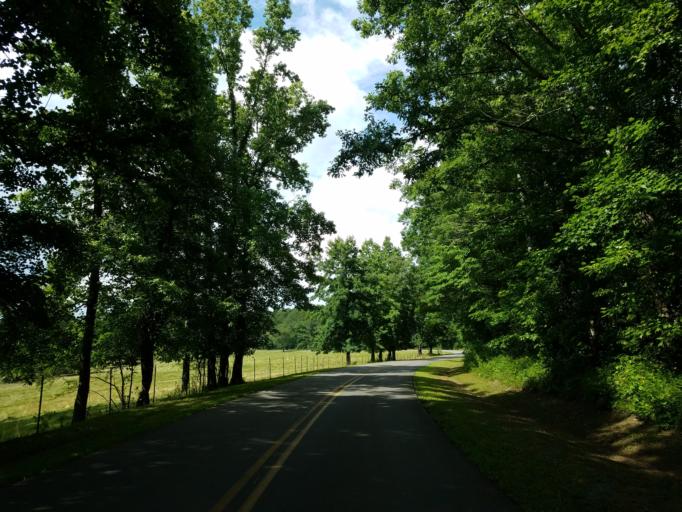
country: US
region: Georgia
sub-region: Pickens County
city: Nelson
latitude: 34.3958
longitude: -84.3757
